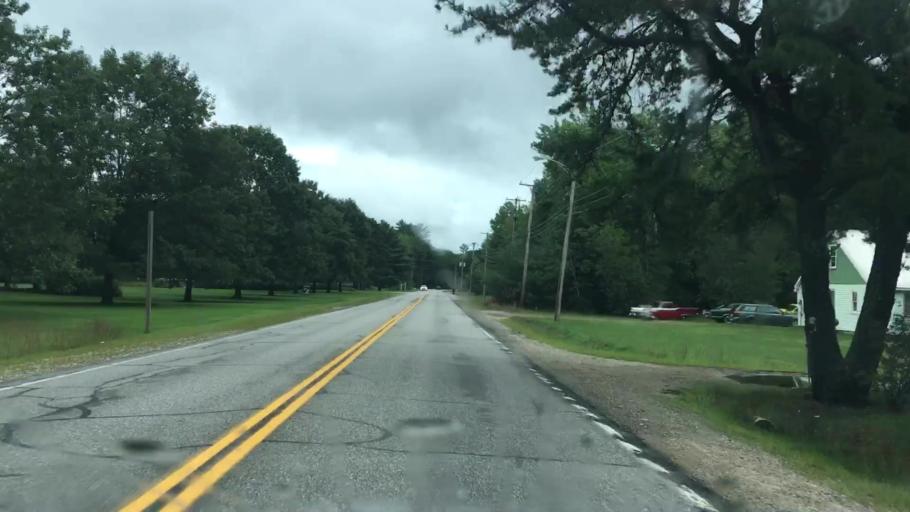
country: US
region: Maine
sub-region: Oxford County
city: Fryeburg
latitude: 44.0110
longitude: -70.9635
